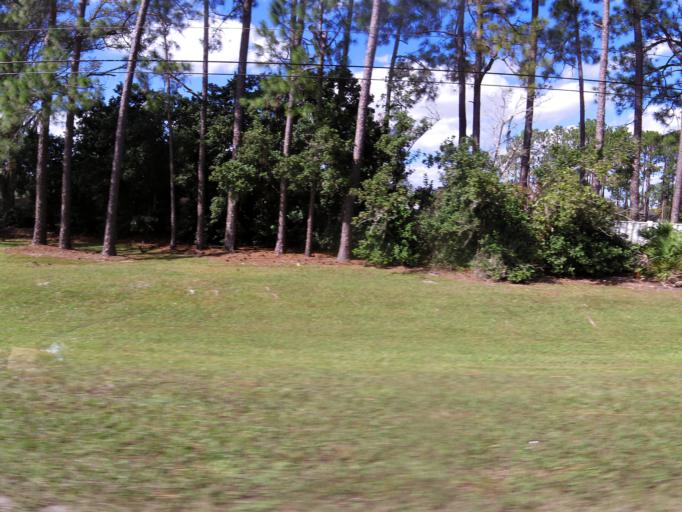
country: US
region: Florida
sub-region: Saint Johns County
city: Fruit Cove
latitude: 30.0544
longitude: -81.5481
